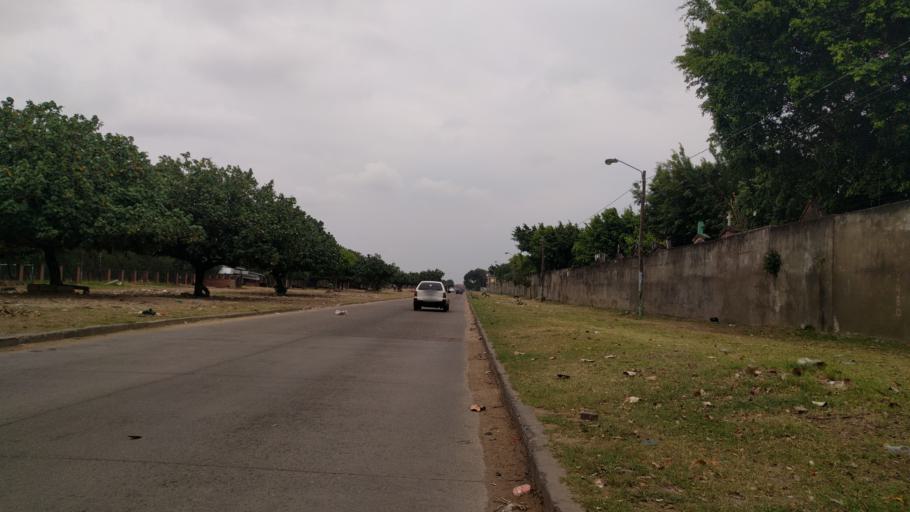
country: BO
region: Santa Cruz
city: Santa Cruz de la Sierra
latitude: -17.8217
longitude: -63.1957
